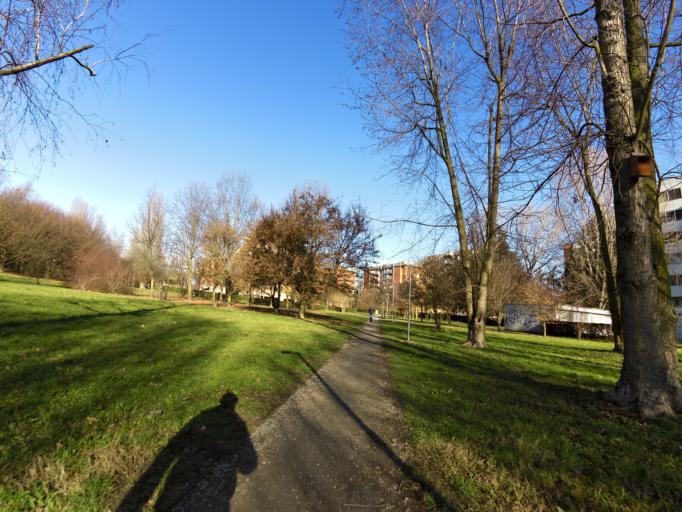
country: IT
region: Lombardy
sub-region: Citta metropolitana di Milano
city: San Giuliano Milanese
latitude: 45.4014
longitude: 9.2855
